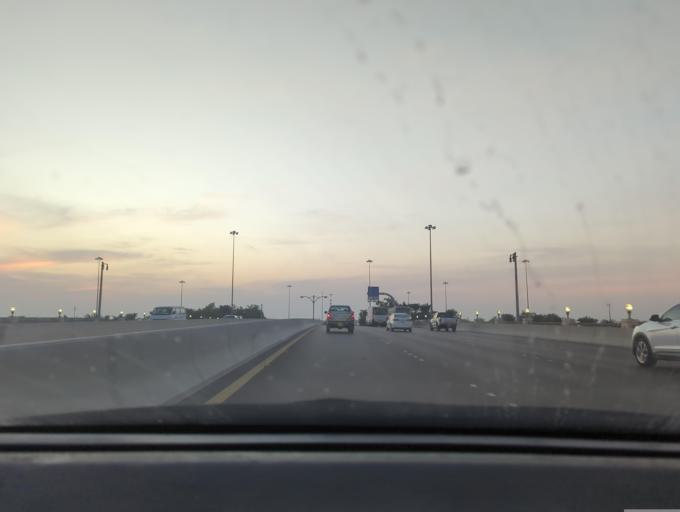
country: AE
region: Abu Dhabi
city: Abu Dhabi
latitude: 24.3738
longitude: 54.5255
